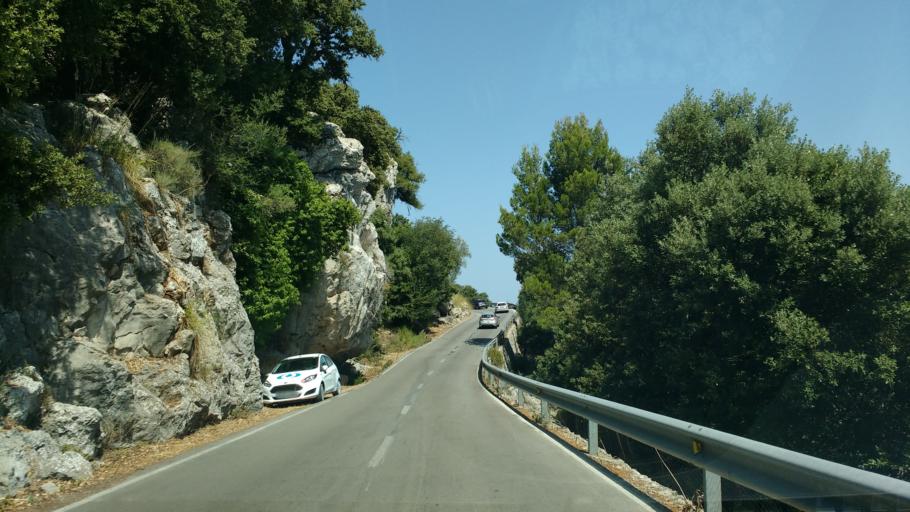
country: ES
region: Balearic Islands
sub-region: Illes Balears
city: Escorca
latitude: 39.8276
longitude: 2.8386
